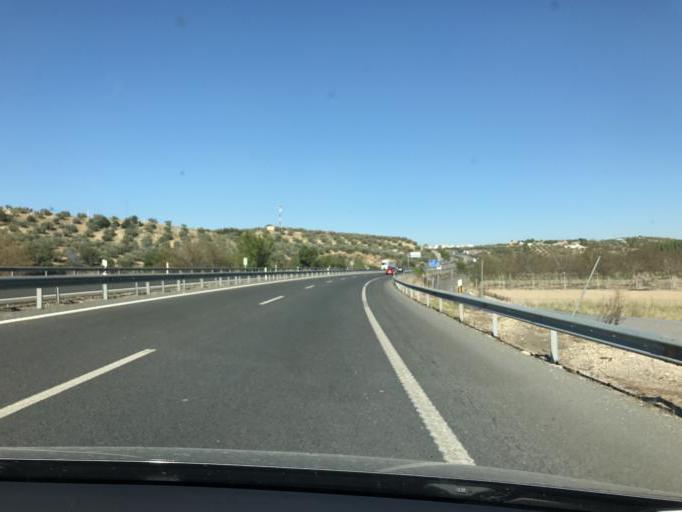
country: ES
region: Andalusia
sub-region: Provincia de Granada
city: Villanueva de Mesia
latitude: 37.1933
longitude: -4.0038
